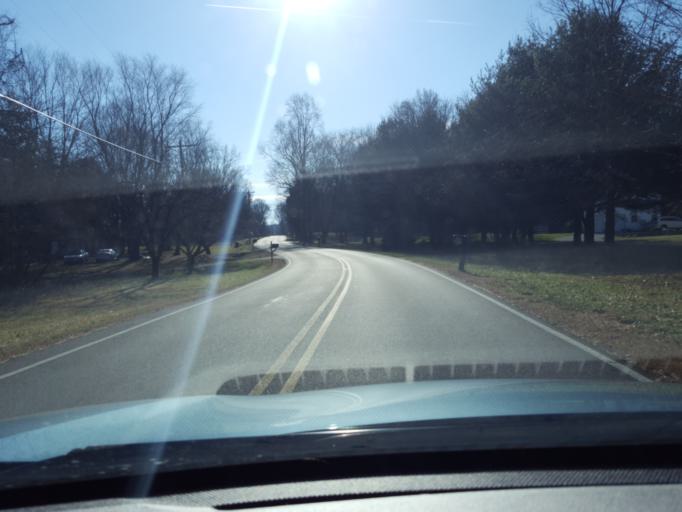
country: US
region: Maryland
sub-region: Calvert County
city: Huntingtown Town Center
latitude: 38.6552
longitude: -76.5769
